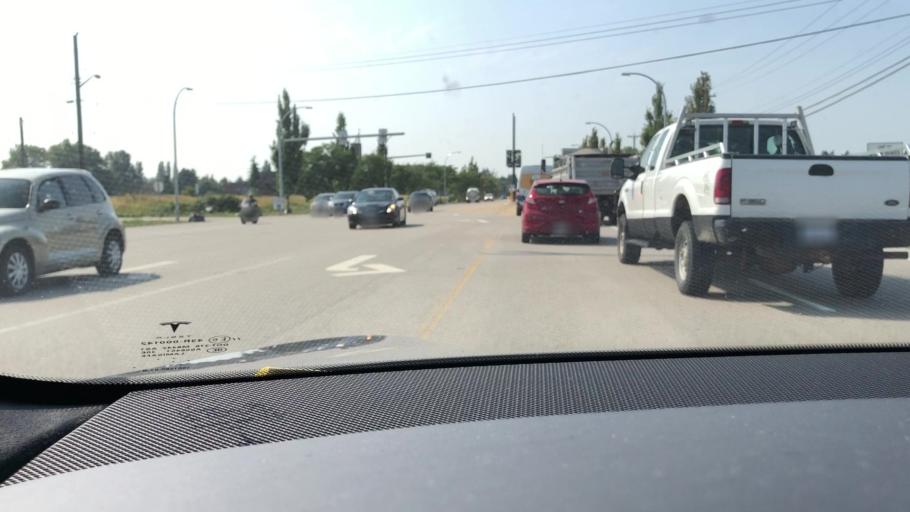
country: CA
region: British Columbia
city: Ladner
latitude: 49.0415
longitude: -123.0688
